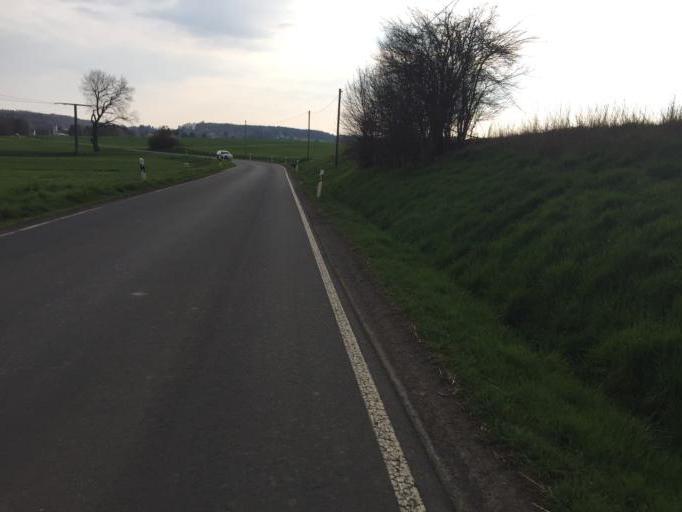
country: DE
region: Hesse
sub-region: Regierungsbezirk Giessen
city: Laubach
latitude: 50.5559
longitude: 8.9567
